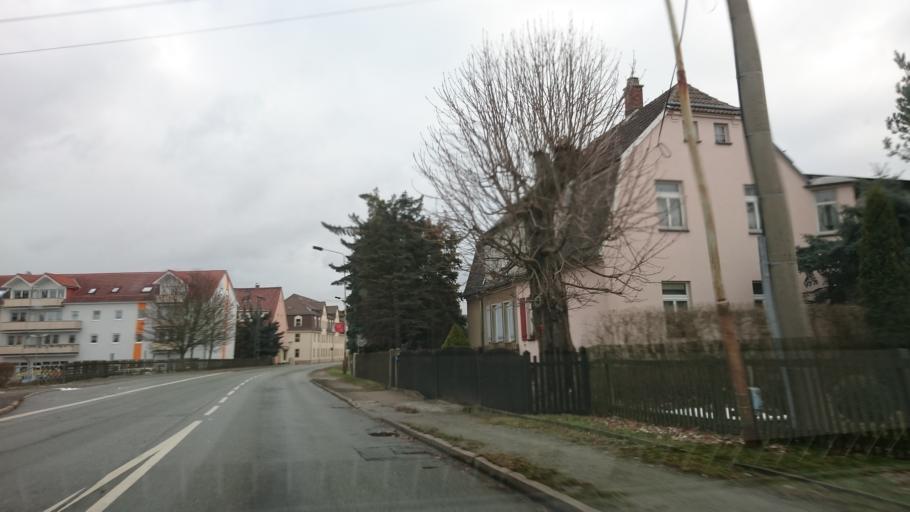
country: DE
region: Saxony
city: Werdau
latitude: 50.7341
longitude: 12.3959
